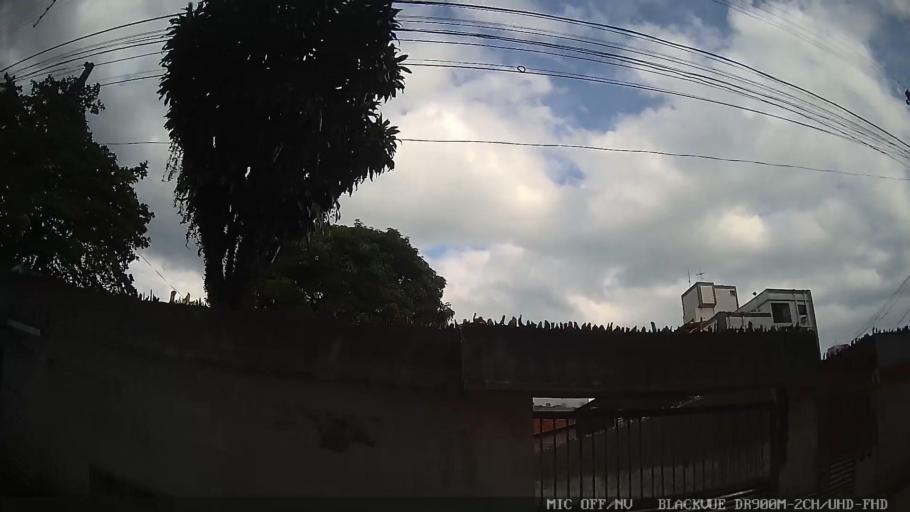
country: BR
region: Sao Paulo
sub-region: Guaruja
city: Guaruja
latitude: -23.9810
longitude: -46.2388
